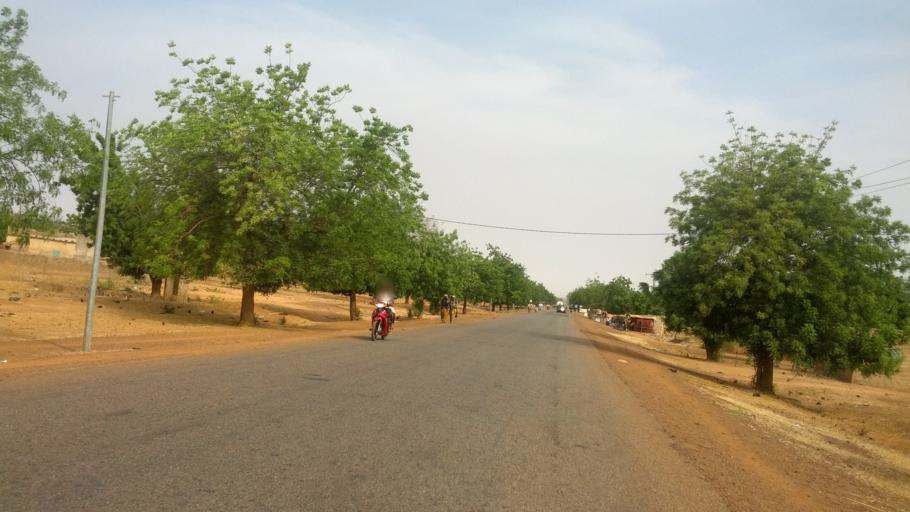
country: BF
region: Centre-Nord
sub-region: Province du Sanmatenga
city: Kaya
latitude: 12.9070
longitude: -1.0783
